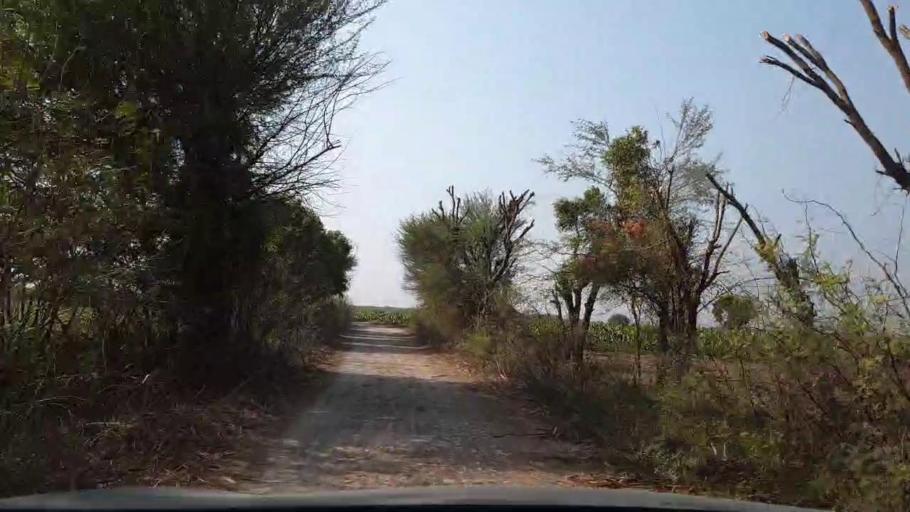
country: PK
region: Sindh
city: Tando Allahyar
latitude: 25.5531
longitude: 68.7850
